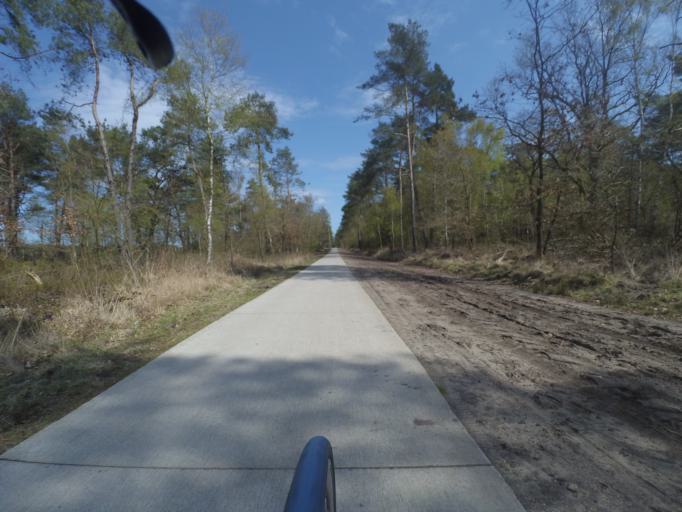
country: NL
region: Gelderland
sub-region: Gemeente Epe
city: Emst
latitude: 52.3332
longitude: 5.9010
